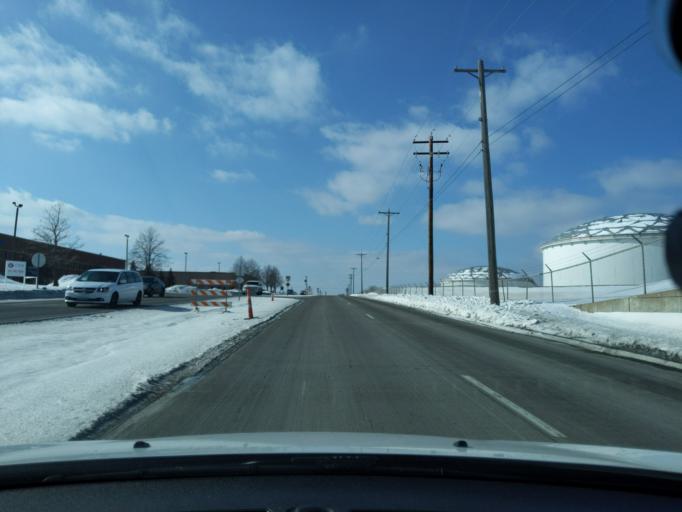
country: US
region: Minnesota
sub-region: Hennepin County
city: Saint Anthony
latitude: 45.0207
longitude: -93.1989
